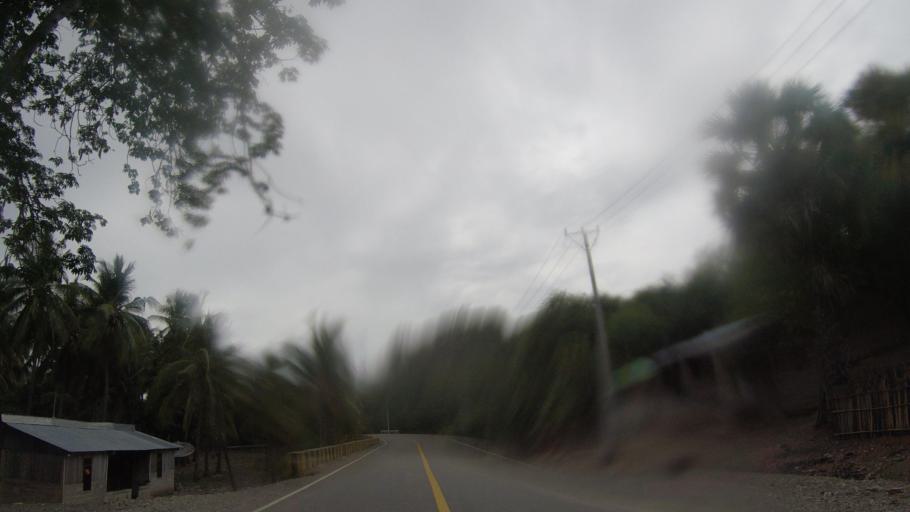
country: TL
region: Lautem
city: Lospalos
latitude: -8.4127
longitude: 126.7408
